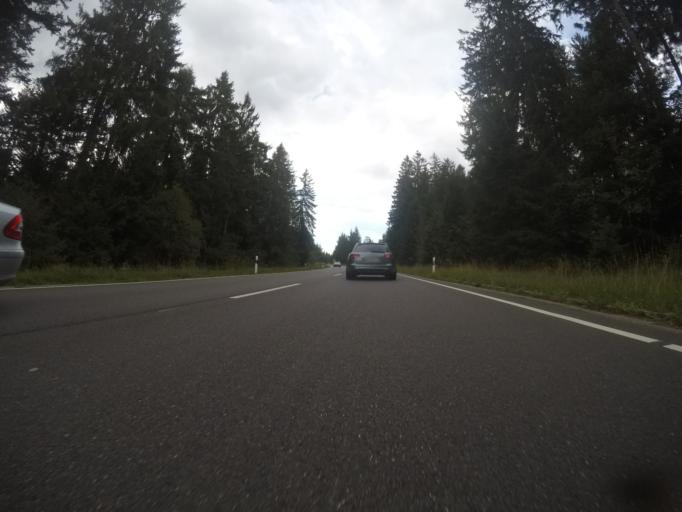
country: DE
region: Baden-Wuerttemberg
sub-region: Freiburg Region
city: Bad Peterstal-Griesbach
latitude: 48.4943
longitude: 8.2483
